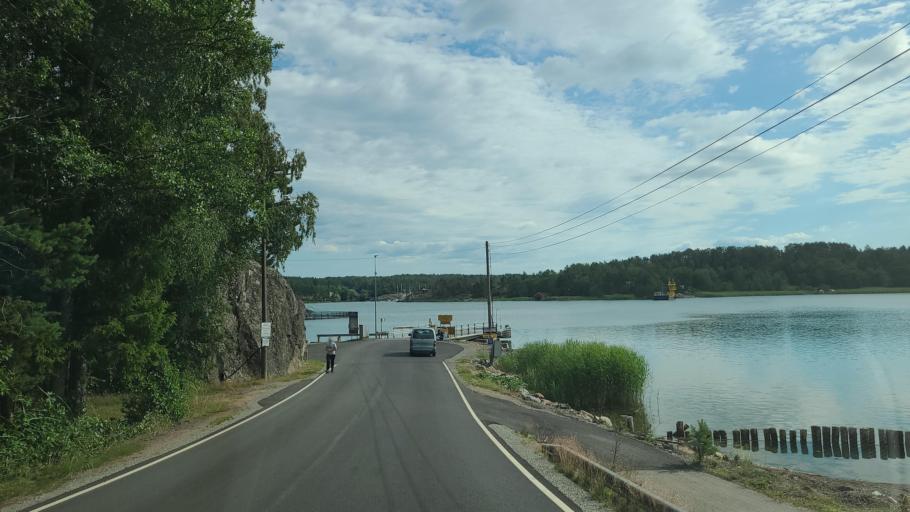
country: FI
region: Varsinais-Suomi
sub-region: Turku
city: Rymaettylae
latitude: 60.3170
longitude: 21.9633
